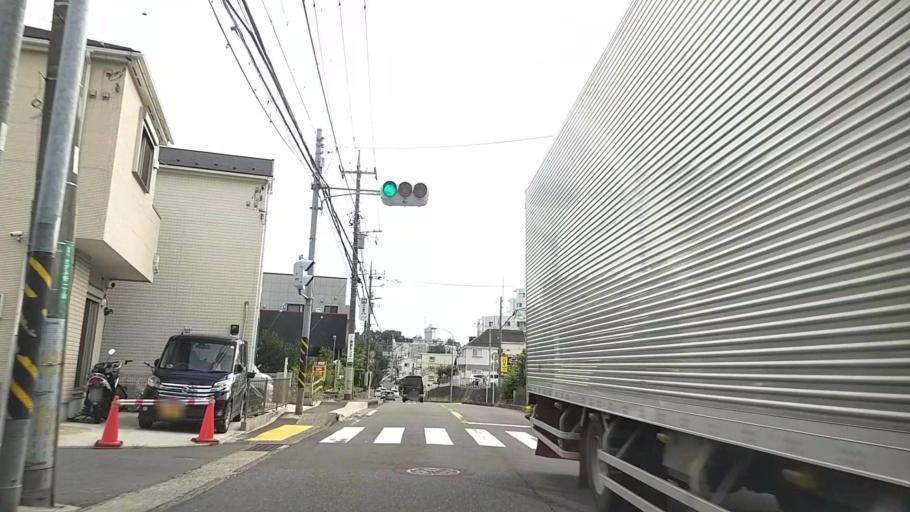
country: JP
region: Kanagawa
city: Minami-rinkan
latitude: 35.4711
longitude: 139.4221
